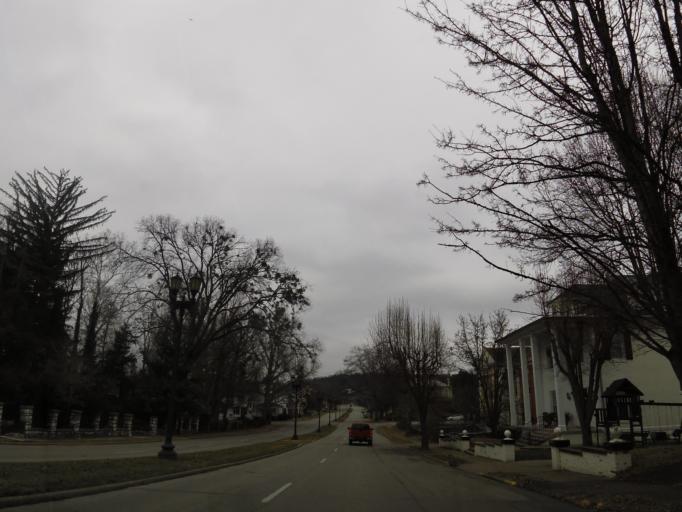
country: US
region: Kentucky
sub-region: Franklin County
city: Frankfort
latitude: 38.1911
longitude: -84.8748
